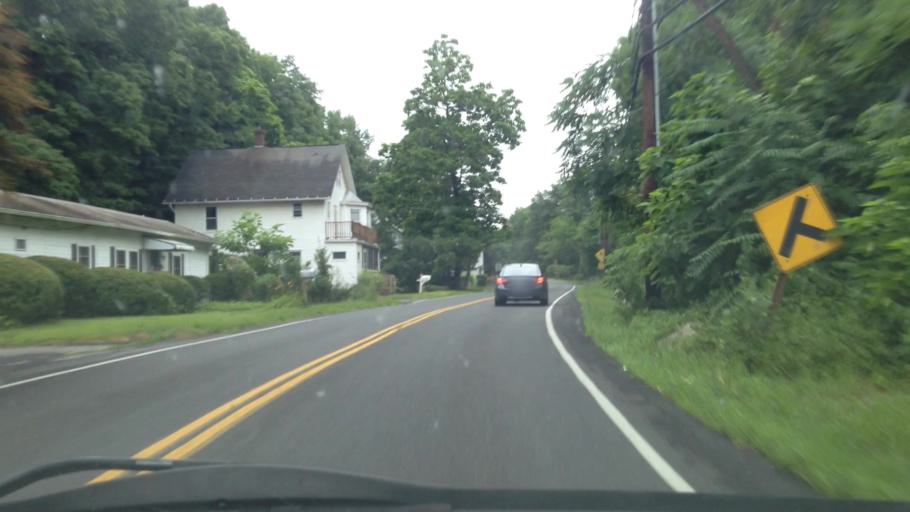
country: US
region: New York
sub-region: Ulster County
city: Highland
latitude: 41.7306
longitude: -73.9714
